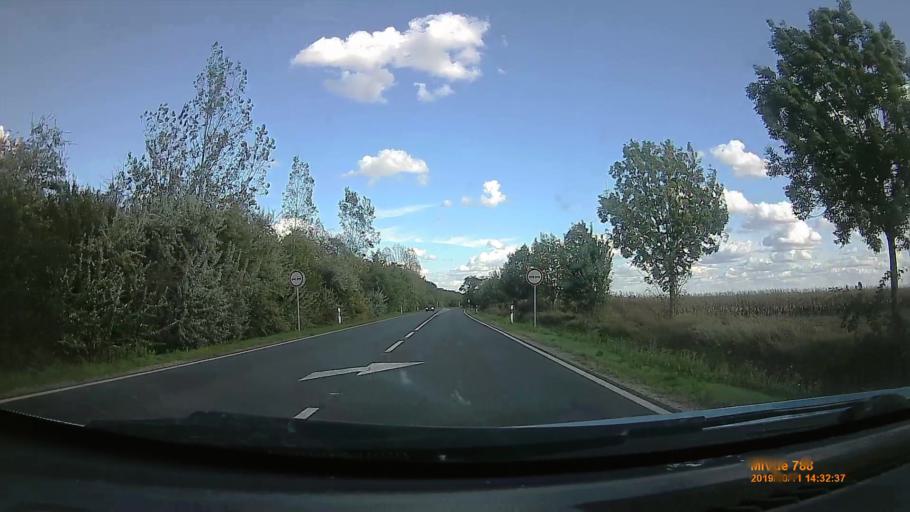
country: HU
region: Hajdu-Bihar
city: Balmazujvaros
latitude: 47.5623
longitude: 21.4410
